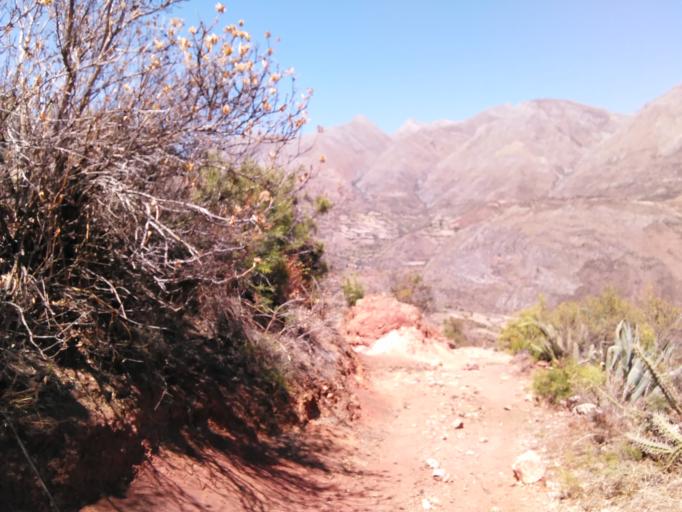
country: PE
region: Ayacucho
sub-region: Provincia de Victor Fajardo
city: Canaria
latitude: -13.8824
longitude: -73.9492
